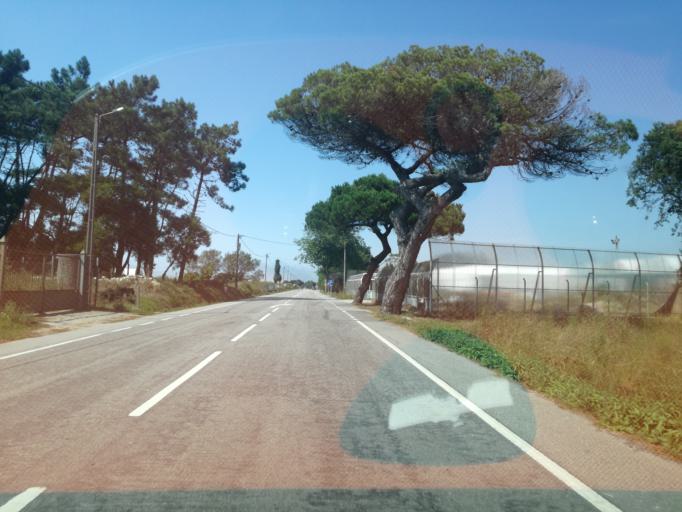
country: PT
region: Braga
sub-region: Esposende
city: Apulia
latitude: 41.4969
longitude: -8.7571
